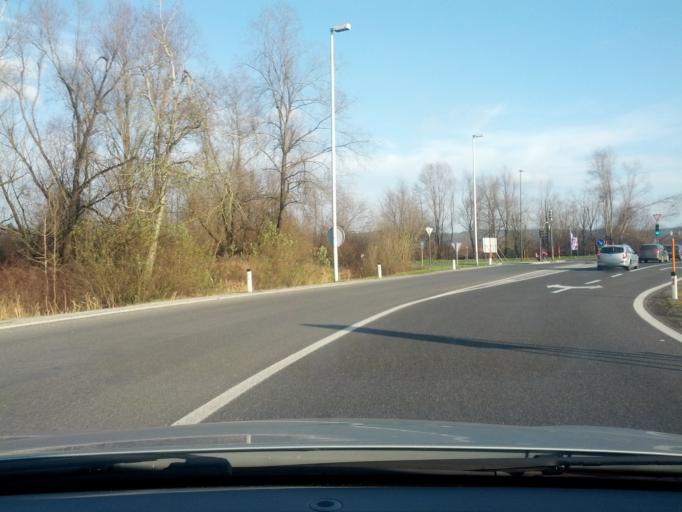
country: SI
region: Ljubljana
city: Ljubljana
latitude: 46.0277
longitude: 14.4980
